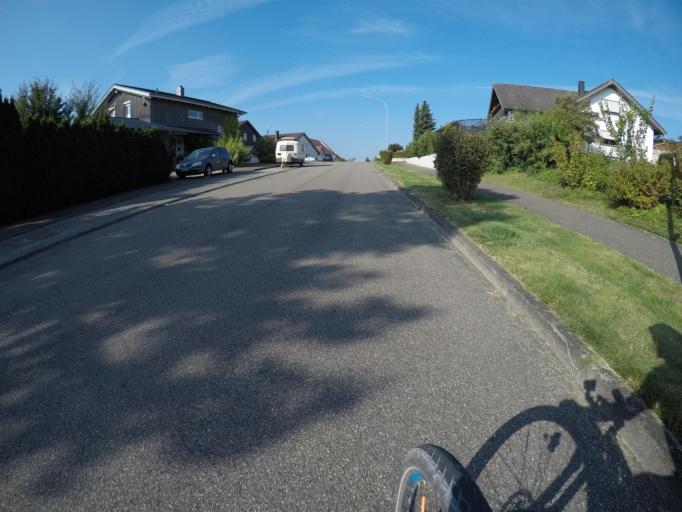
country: DE
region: Baden-Wuerttemberg
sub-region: Regierungsbezirk Stuttgart
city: Gerstetten
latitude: 48.6261
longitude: 10.0052
